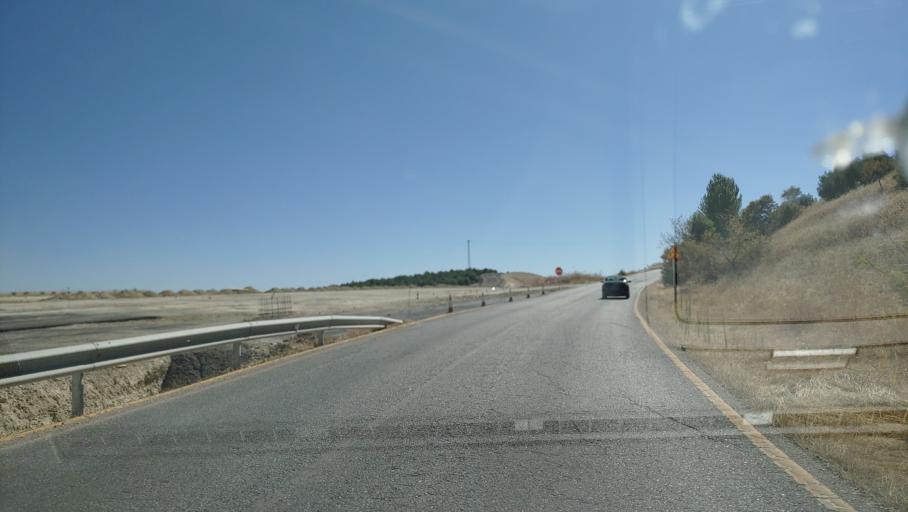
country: ES
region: Andalusia
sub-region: Provincia de Jaen
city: Iznatoraf
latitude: 38.1495
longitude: -3.0212
